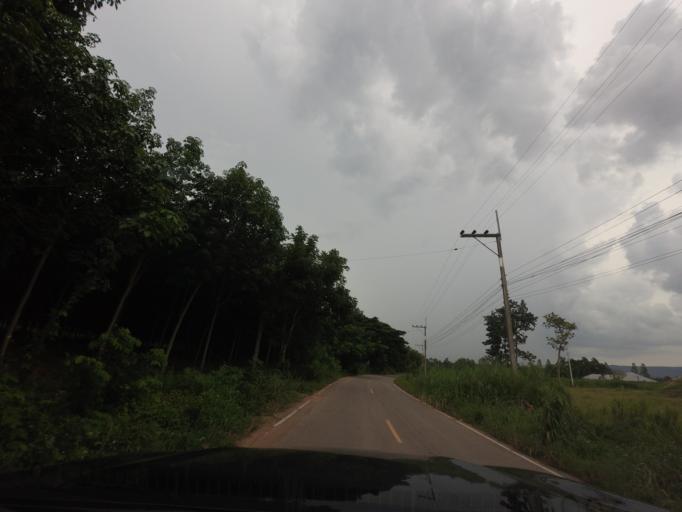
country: TH
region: Khon Kaen
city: Wiang Kao
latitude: 16.6801
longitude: 102.2737
